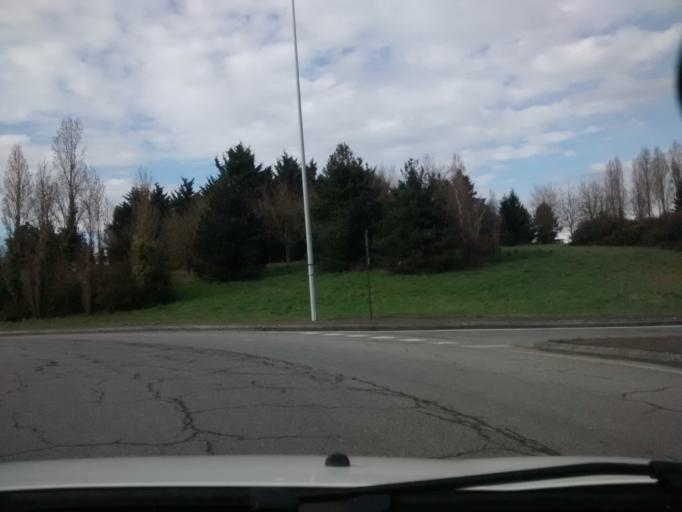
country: FR
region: Brittany
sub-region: Departement d'Ille-et-Vilaine
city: Cesson-Sevigne
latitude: 48.1108
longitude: -1.5847
